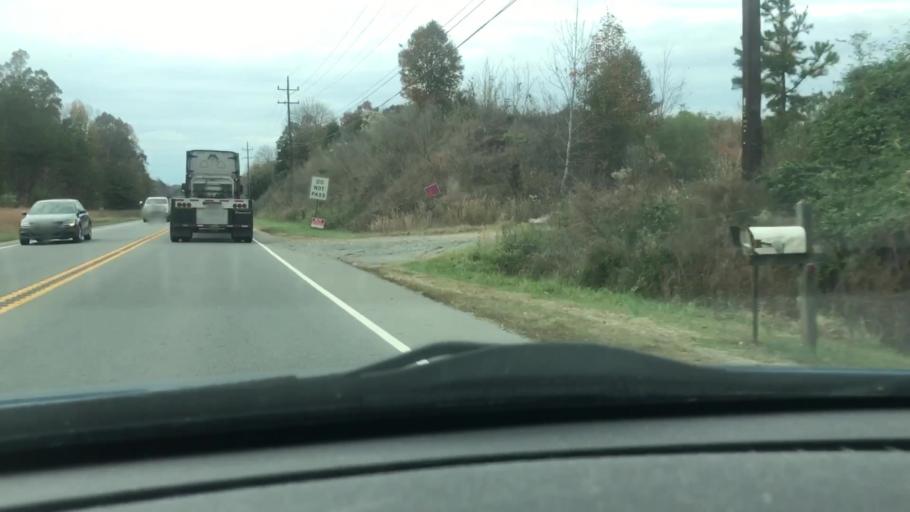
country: US
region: North Carolina
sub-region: Davidson County
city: Lexington
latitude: 35.8061
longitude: -80.1708
